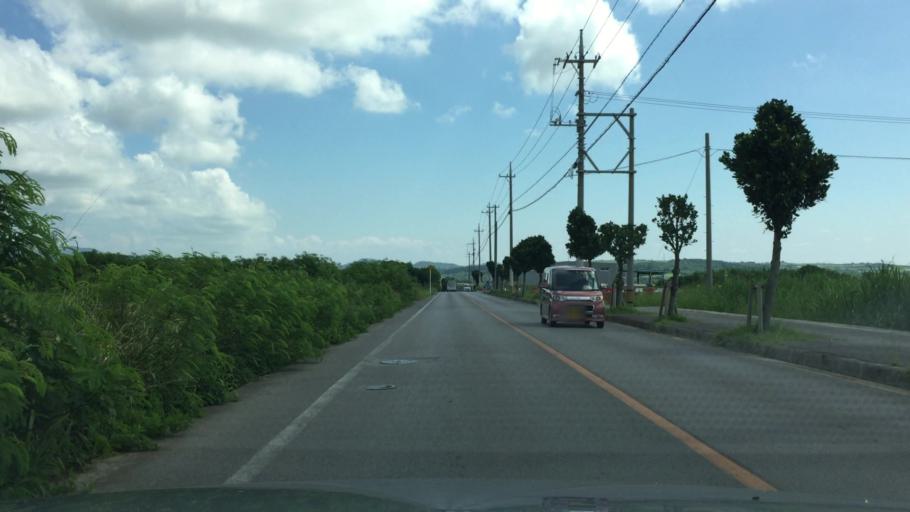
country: JP
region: Okinawa
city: Ishigaki
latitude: 24.3516
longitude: 124.1886
